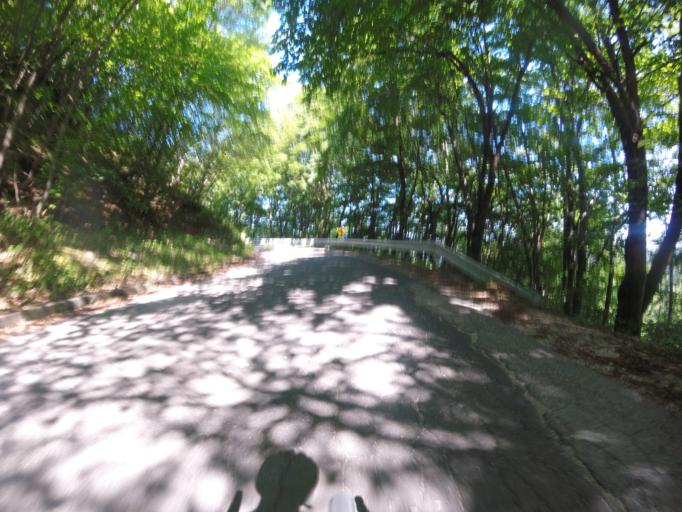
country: SI
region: Brezice
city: Brezice
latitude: 45.8215
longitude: 15.5444
